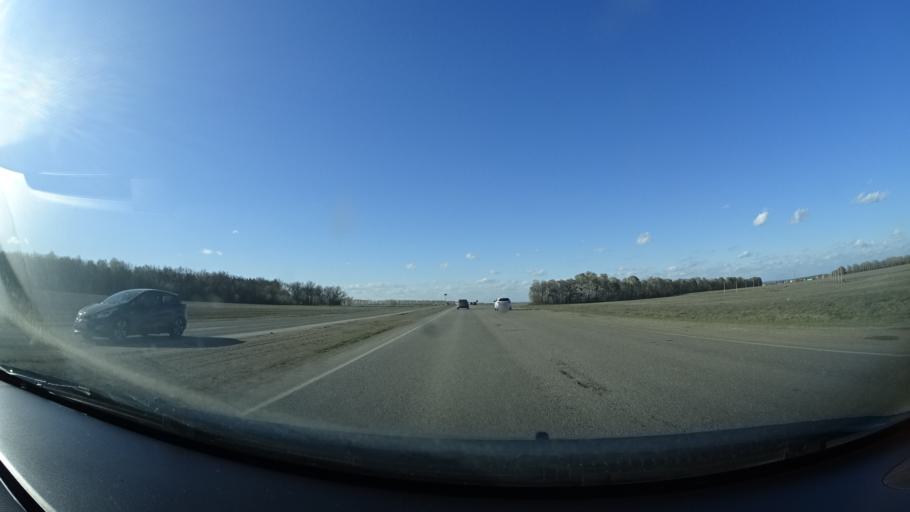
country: RU
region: Bashkortostan
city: Kabakovo
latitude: 54.4599
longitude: 55.9159
